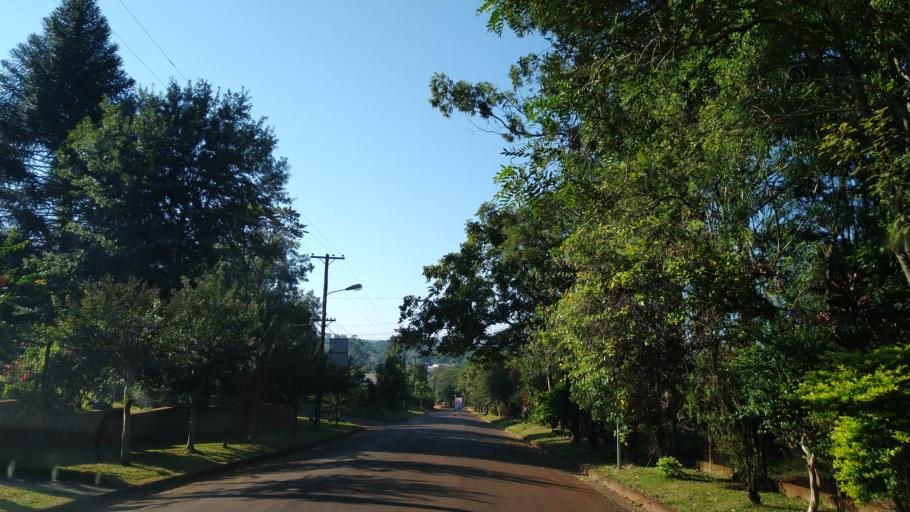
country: AR
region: Misiones
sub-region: Departamento de Montecarlo
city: Montecarlo
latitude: -26.5600
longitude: -54.7769
